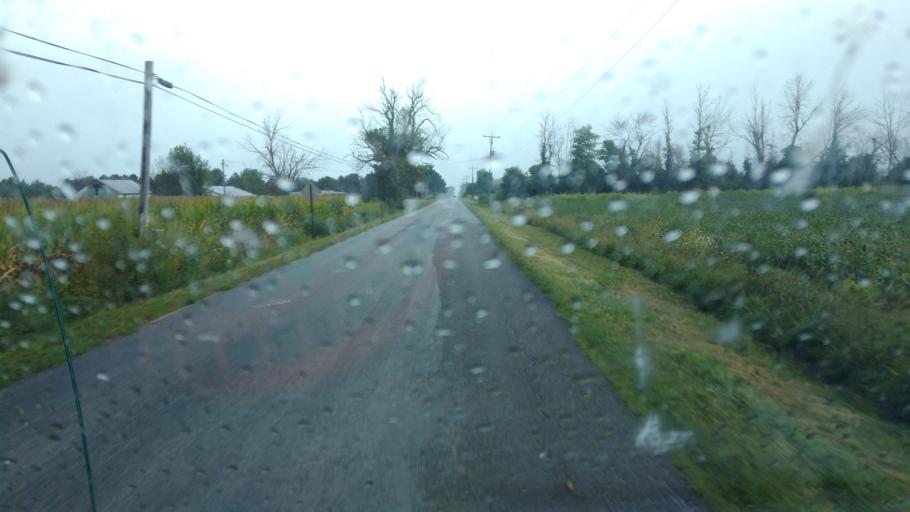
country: US
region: Ohio
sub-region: Hardin County
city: Kenton
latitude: 40.6726
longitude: -83.5380
